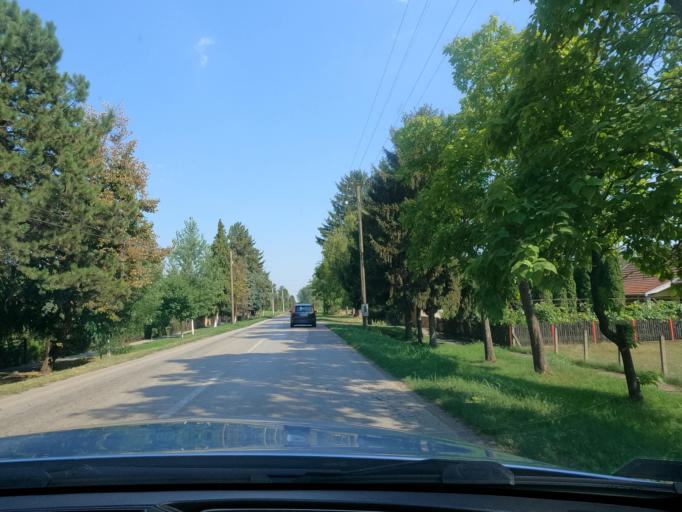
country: RS
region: Autonomna Pokrajina Vojvodina
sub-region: Severnobacki Okrug
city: Mali Igos
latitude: 45.7613
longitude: 19.7555
